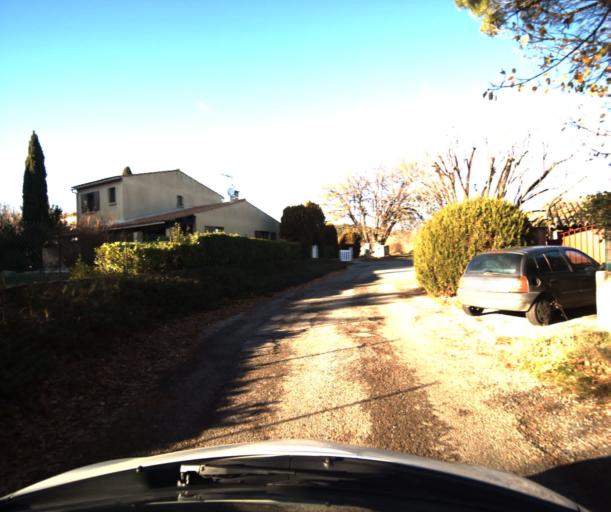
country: FR
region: Provence-Alpes-Cote d'Azur
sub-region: Departement du Vaucluse
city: Pertuis
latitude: 43.7074
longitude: 5.4939
